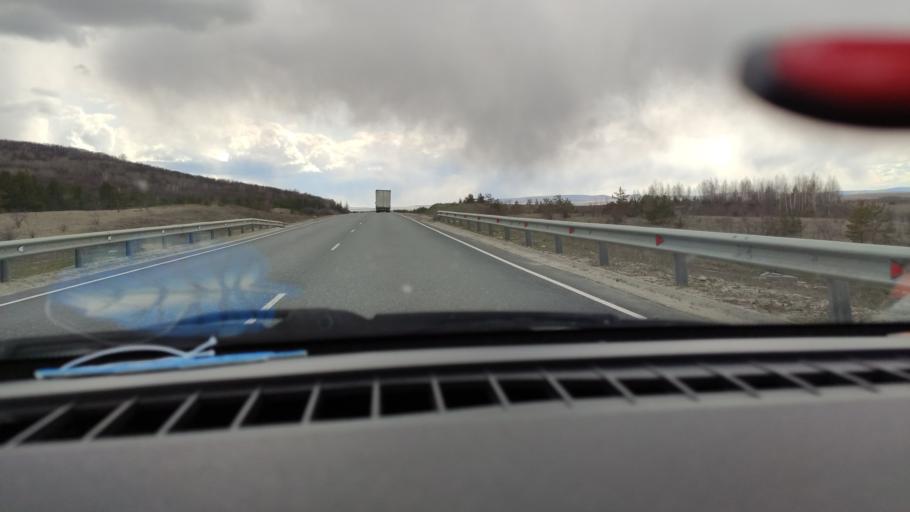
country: RU
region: Saratov
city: Alekseyevka
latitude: 52.3948
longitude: 47.9815
